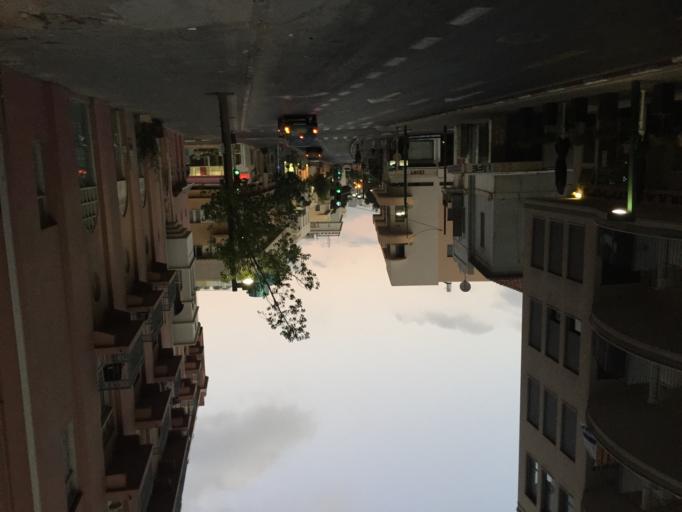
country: IL
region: Tel Aviv
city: Tel Aviv
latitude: 32.0638
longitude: 34.7708
